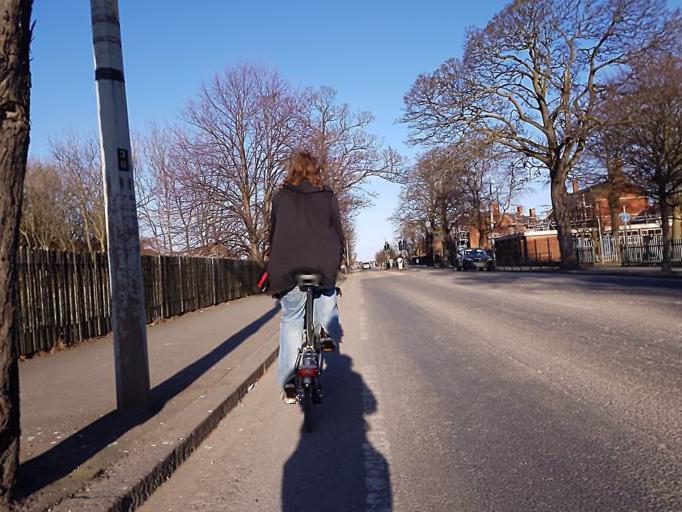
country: GB
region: England
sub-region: North East Lincolnshire
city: Cleethorpes
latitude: 53.5547
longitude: -0.0527
